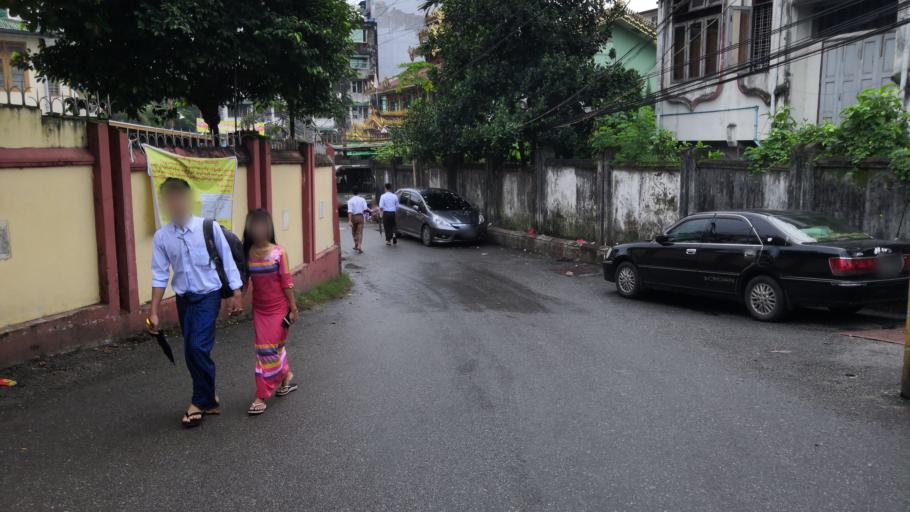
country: MM
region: Yangon
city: Yangon
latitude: 16.7982
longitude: 96.1543
